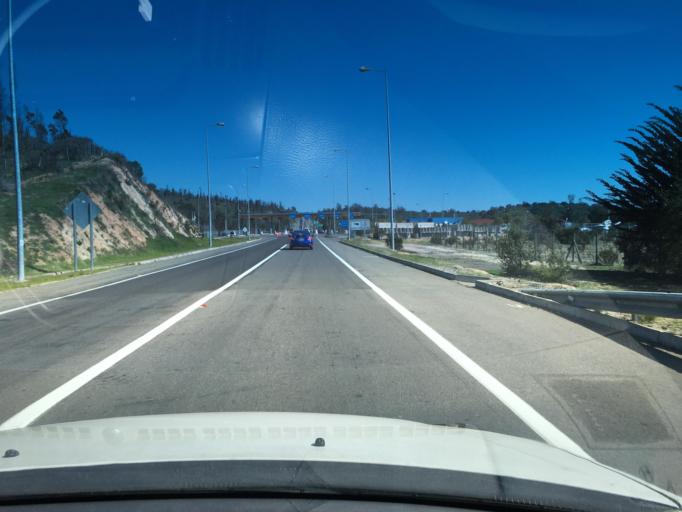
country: CL
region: Valparaiso
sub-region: San Antonio Province
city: El Tabo
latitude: -33.3992
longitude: -71.4958
